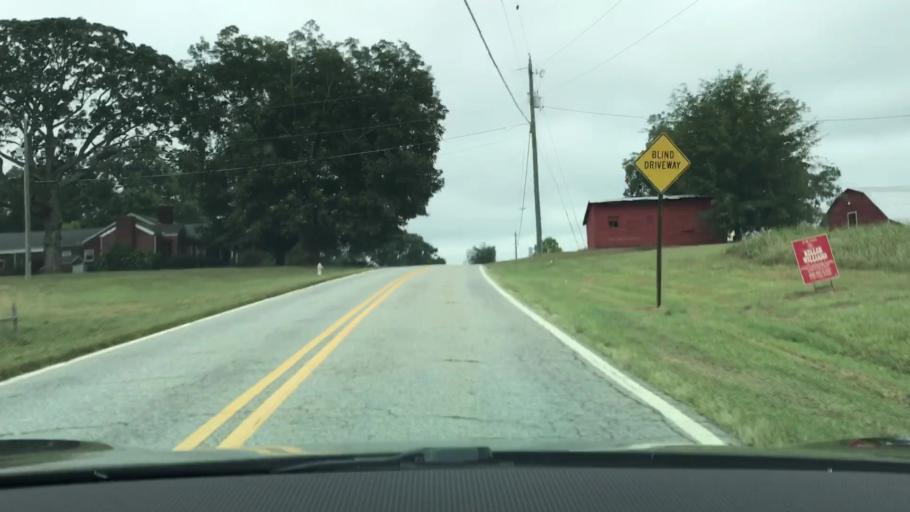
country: US
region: Georgia
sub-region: Barrow County
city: Auburn
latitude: 34.0452
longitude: -83.8100
